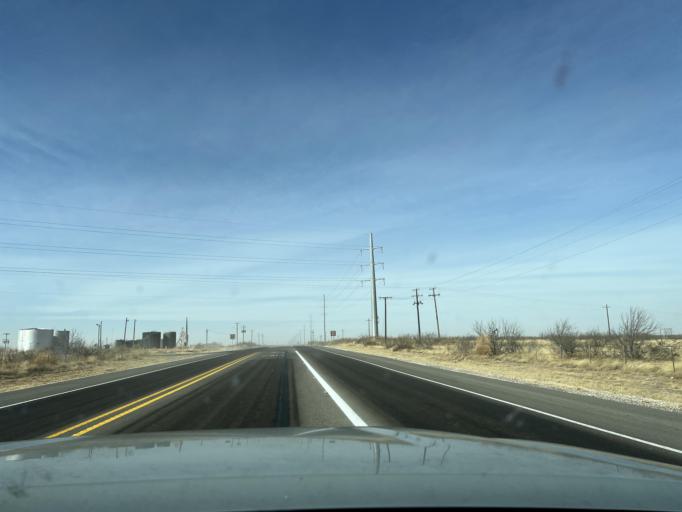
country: US
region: Texas
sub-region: Andrews County
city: Andrews
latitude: 32.3336
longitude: -102.6567
